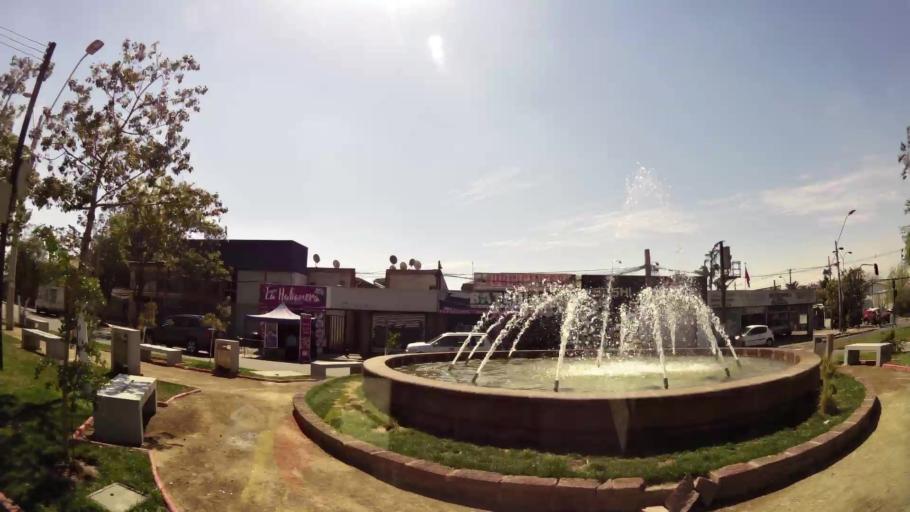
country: CL
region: Santiago Metropolitan
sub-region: Provincia de Santiago
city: La Pintana
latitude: -33.5283
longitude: -70.6360
